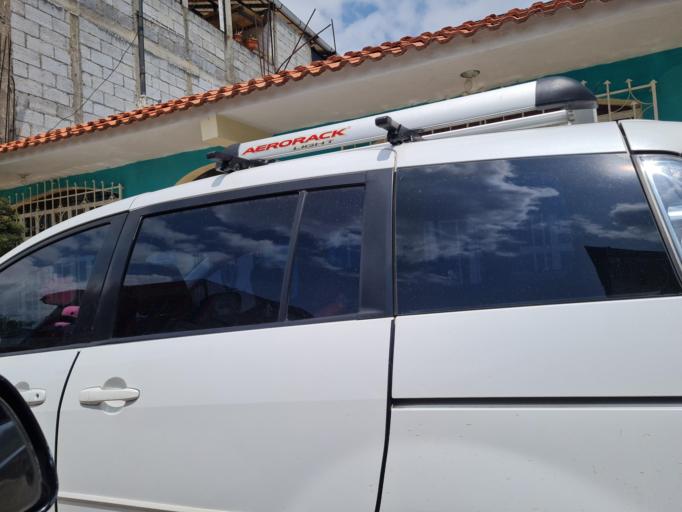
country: GT
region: Quetzaltenango
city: Quetzaltenango
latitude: 14.8295
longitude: -91.5315
